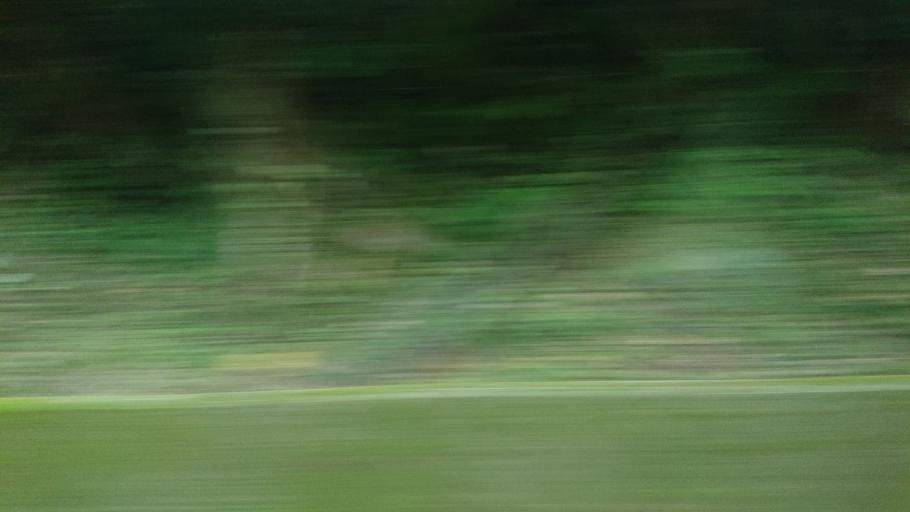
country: TW
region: Taiwan
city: Daxi
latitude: 24.8762
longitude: 121.3823
